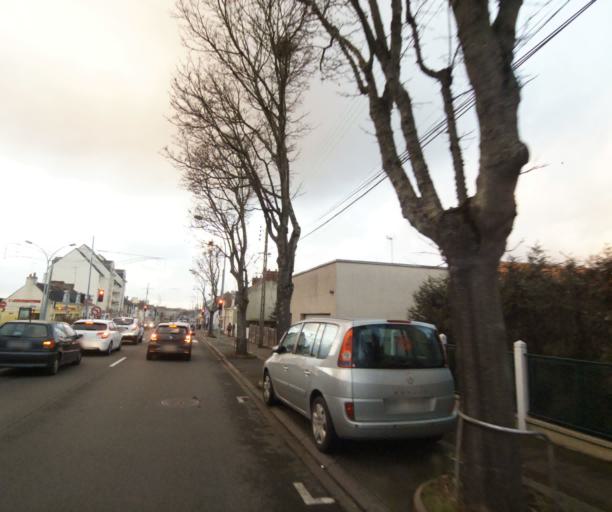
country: FR
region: Pays de la Loire
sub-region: Departement de la Sarthe
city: Le Mans
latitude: 47.9821
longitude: 0.2149
